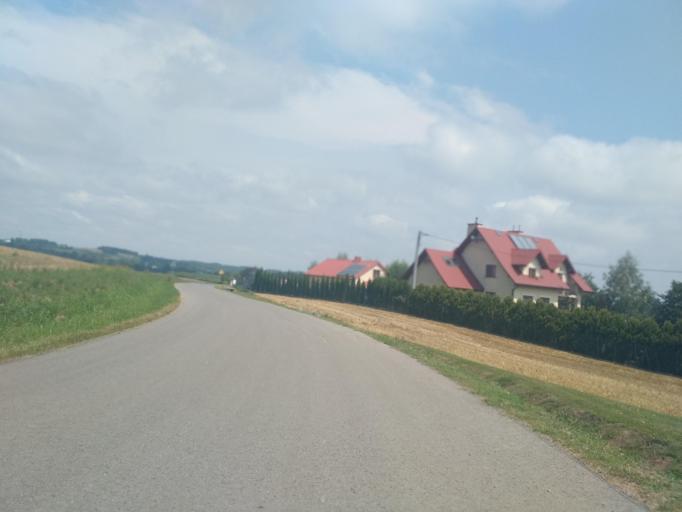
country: PL
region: Subcarpathian Voivodeship
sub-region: Powiat lancucki
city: Kraczkowa
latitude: 50.0273
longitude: 22.1641
